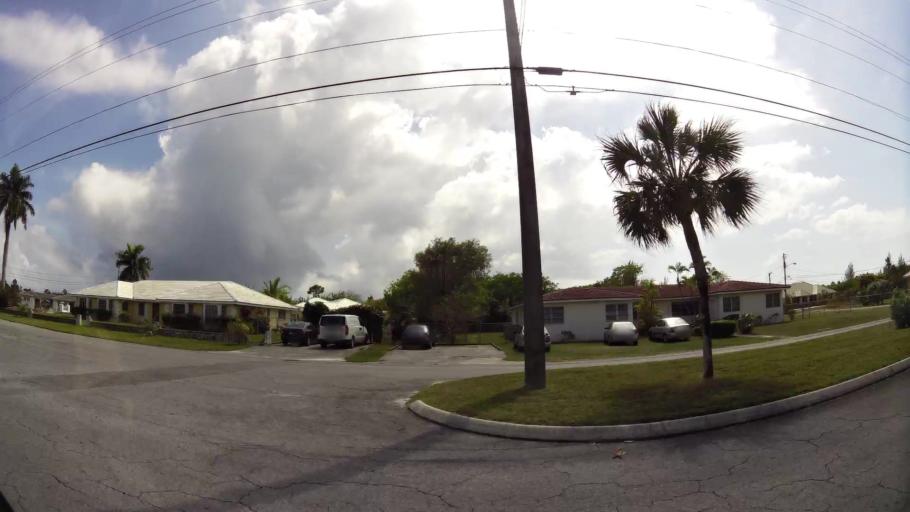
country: BS
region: Freeport
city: Freeport
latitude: 26.5037
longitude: -78.7047
